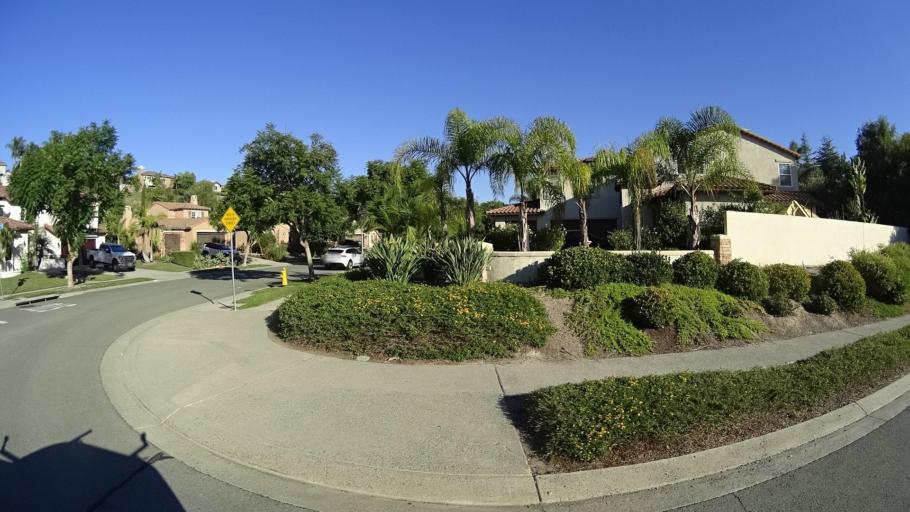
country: US
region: California
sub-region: San Diego County
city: La Presa
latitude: 32.6588
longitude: -116.9443
